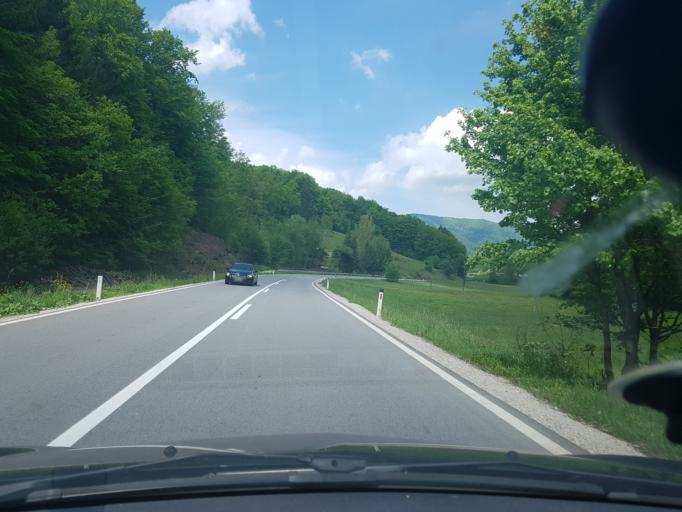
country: SI
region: Rogatec
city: Rogatec
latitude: 46.2308
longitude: 15.6741
